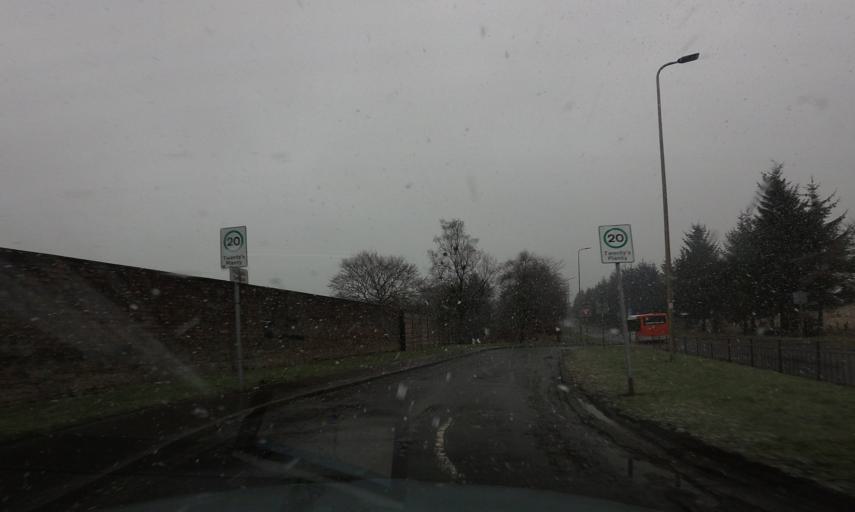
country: GB
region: Scotland
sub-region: North Lanarkshire
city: Caldercruix
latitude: 55.8444
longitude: -3.8683
